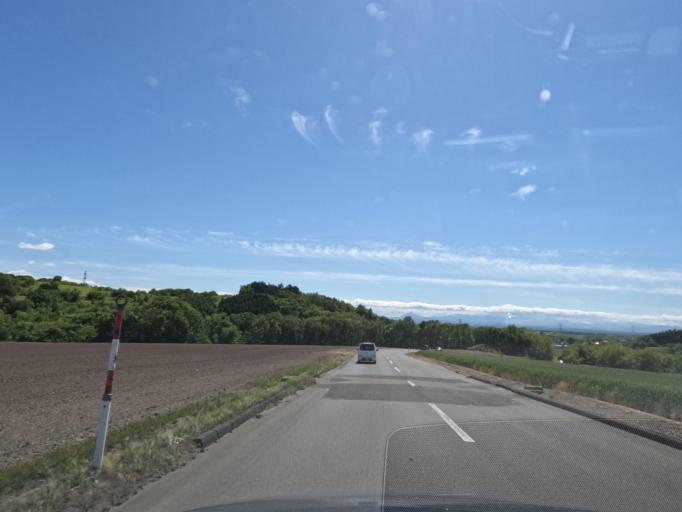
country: JP
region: Hokkaido
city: Iwamizawa
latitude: 43.0907
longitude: 141.7590
